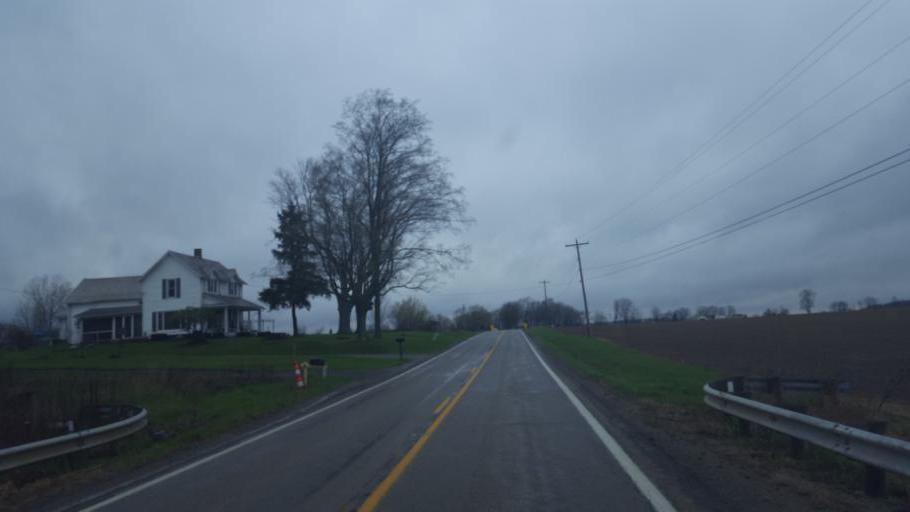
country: US
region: Ohio
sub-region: Morrow County
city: Cardington
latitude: 40.4827
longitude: -82.8425
